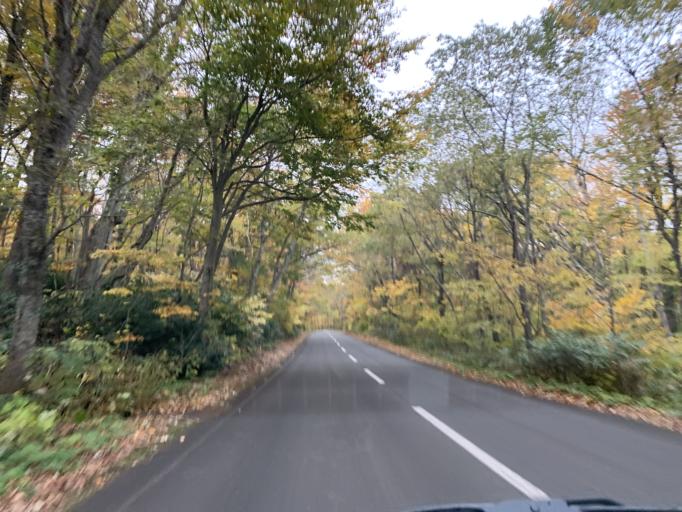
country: JP
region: Iwate
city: Mizusawa
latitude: 39.1063
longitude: 140.8623
